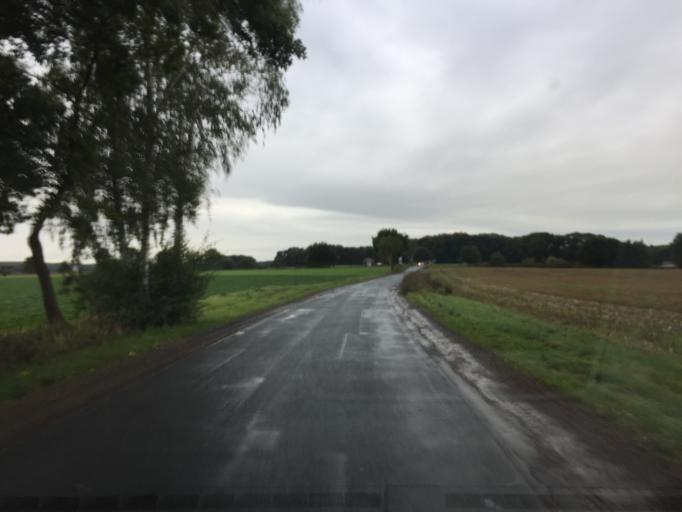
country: DE
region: Lower Saxony
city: Liebenau
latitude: 52.6411
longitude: 9.1027
